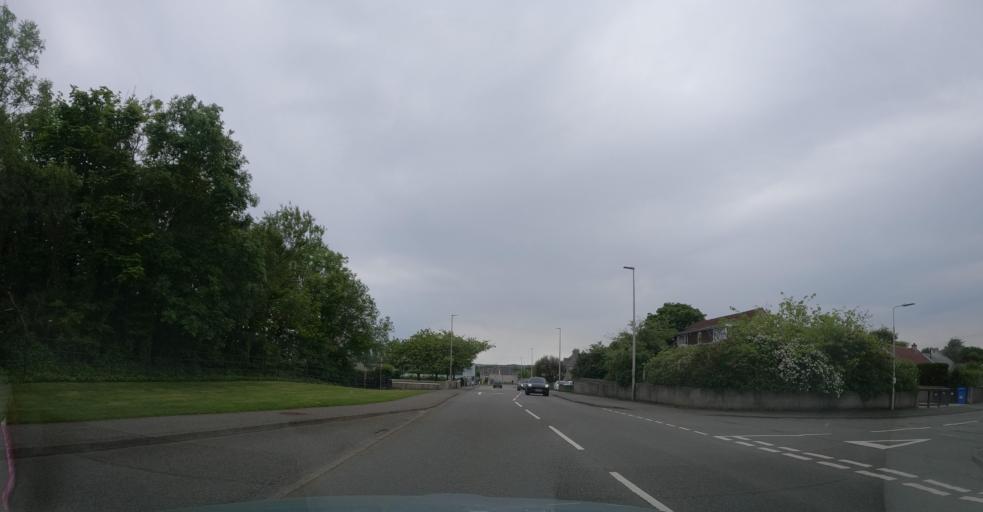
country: GB
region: Scotland
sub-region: Eilean Siar
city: Isle of Lewis
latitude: 58.2208
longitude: -6.3862
